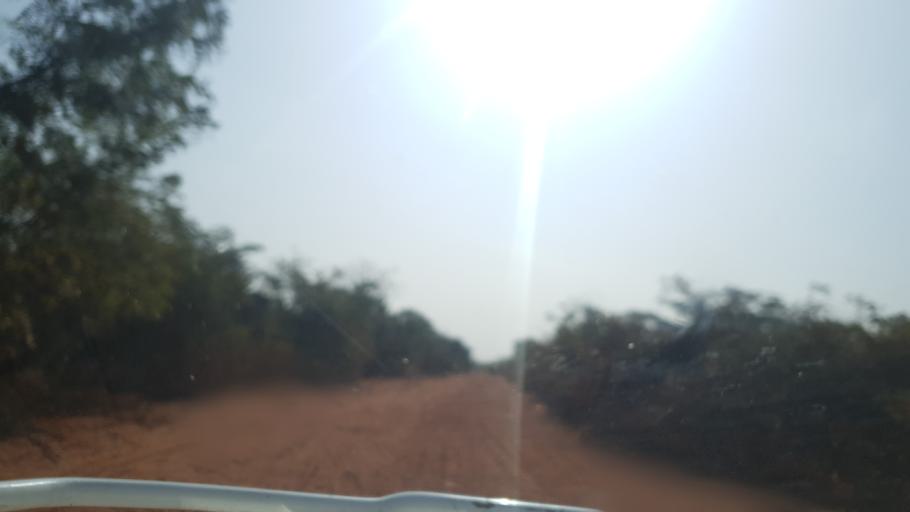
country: ML
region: Koulikoro
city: Dioila
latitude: 12.6964
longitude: -6.7567
